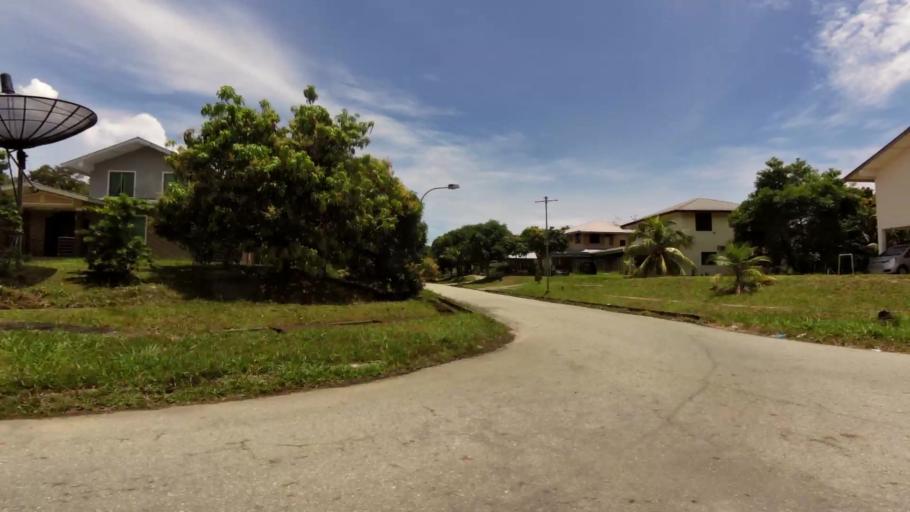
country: BN
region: Brunei and Muara
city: Bandar Seri Begawan
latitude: 4.9633
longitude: 114.9222
